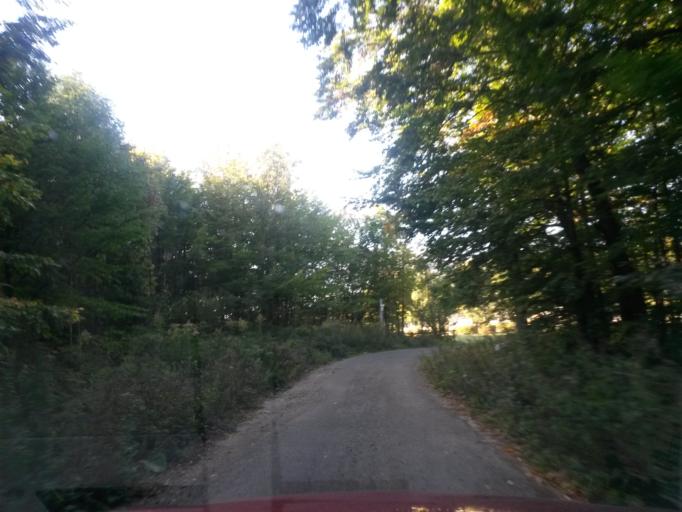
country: SK
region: Kosicky
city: Secovce
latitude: 48.7375
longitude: 21.5355
